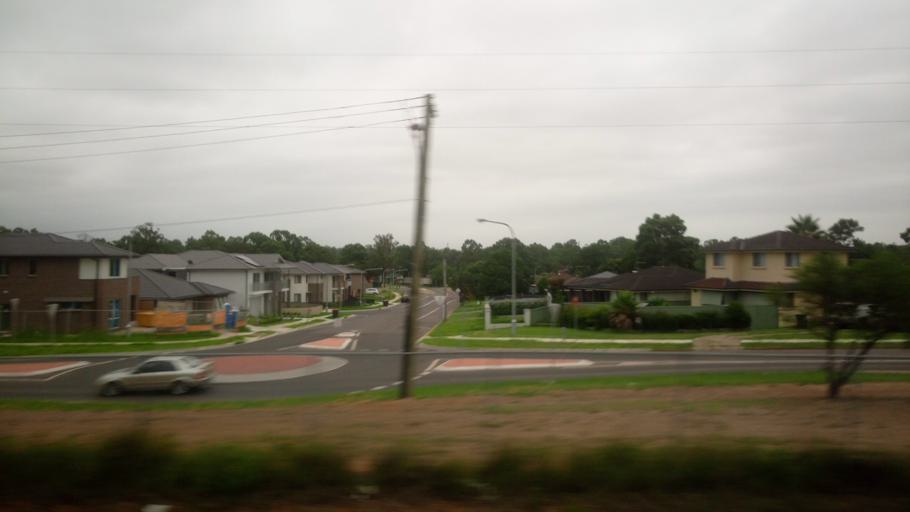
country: AU
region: New South Wales
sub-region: Penrith Municipality
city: Werrington County
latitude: -33.7580
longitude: 150.7402
